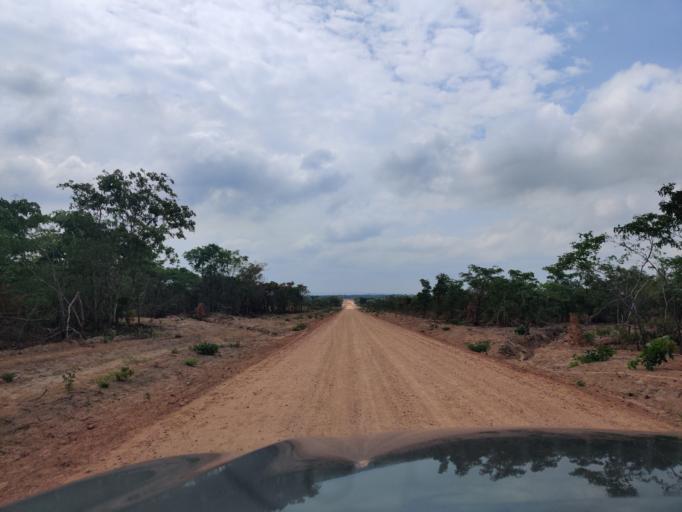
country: ZM
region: Central
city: Mkushi
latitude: -13.6770
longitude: 29.7532
